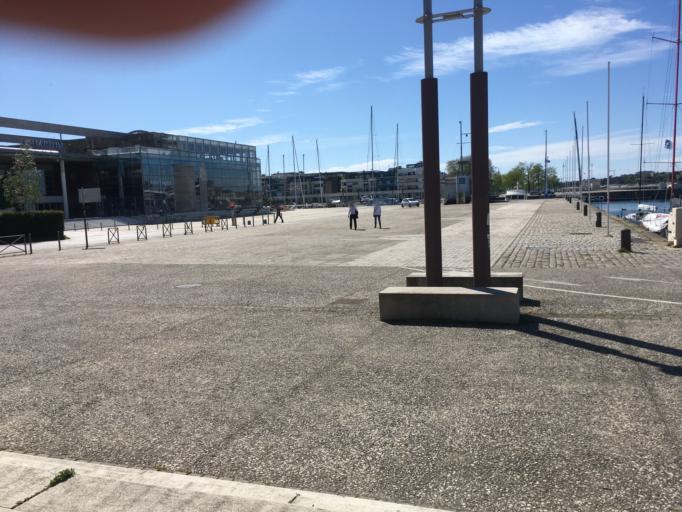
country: FR
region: Poitou-Charentes
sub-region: Departement de la Charente-Maritime
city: La Rochelle
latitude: 46.1543
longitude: -1.1496
